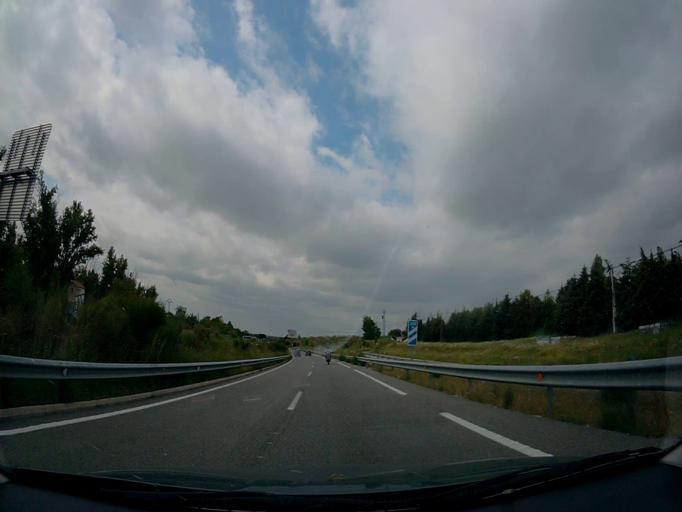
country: ES
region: Madrid
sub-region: Provincia de Madrid
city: Villaviciosa de Odon
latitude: 40.3864
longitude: -3.9030
